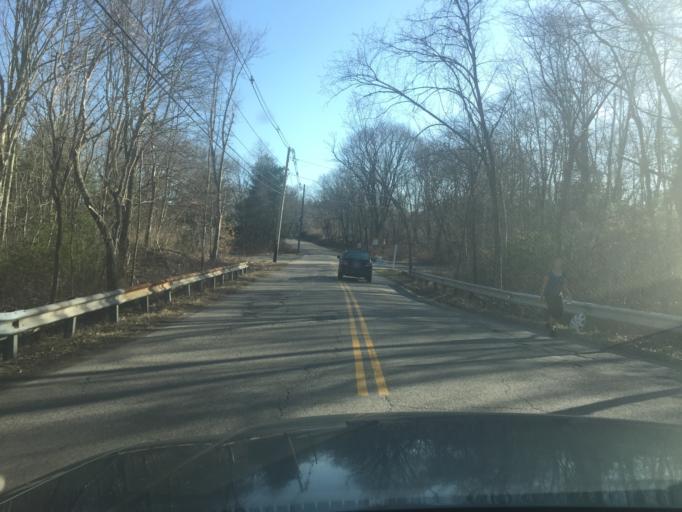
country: US
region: Massachusetts
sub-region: Norfolk County
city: Millis-Clicquot
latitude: 42.1323
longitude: -71.3612
